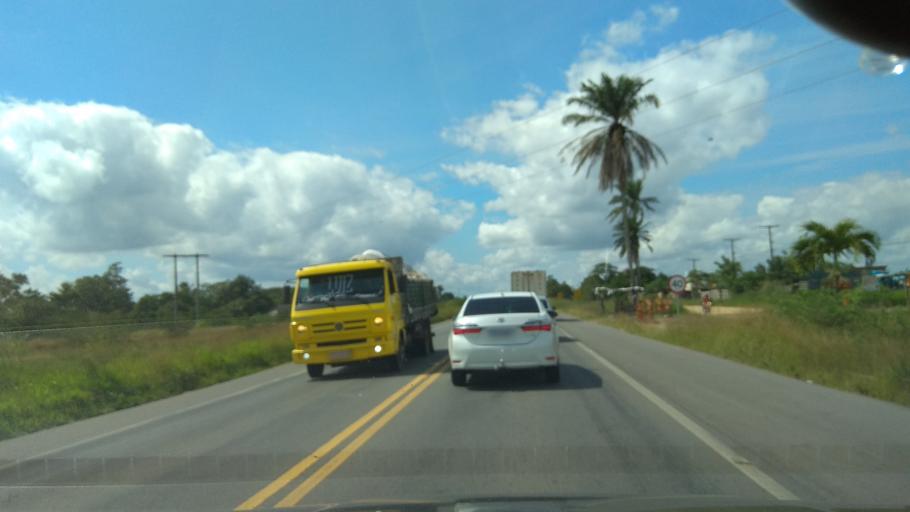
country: BR
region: Bahia
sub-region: Cruz Das Almas
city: Cruz das Almas
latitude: -12.6104
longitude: -39.0808
